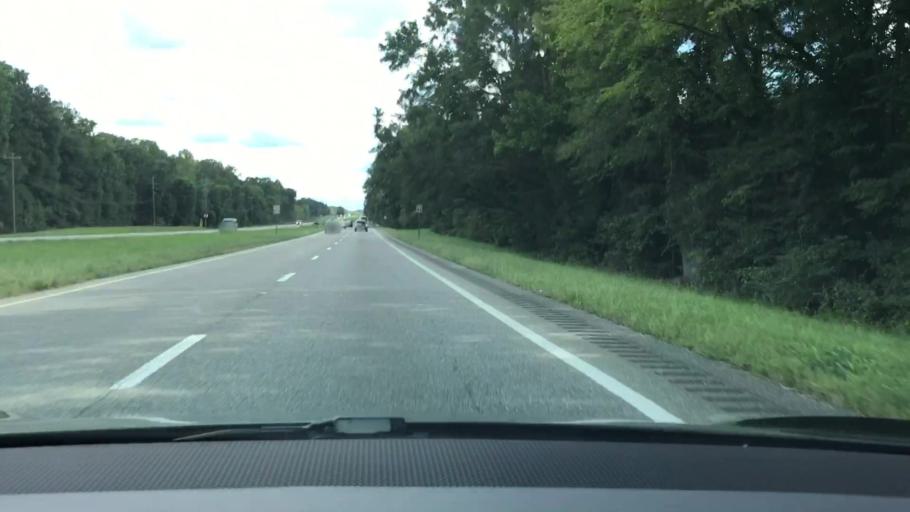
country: US
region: Alabama
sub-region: Montgomery County
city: Pike Road
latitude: 32.1893
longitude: -86.1176
